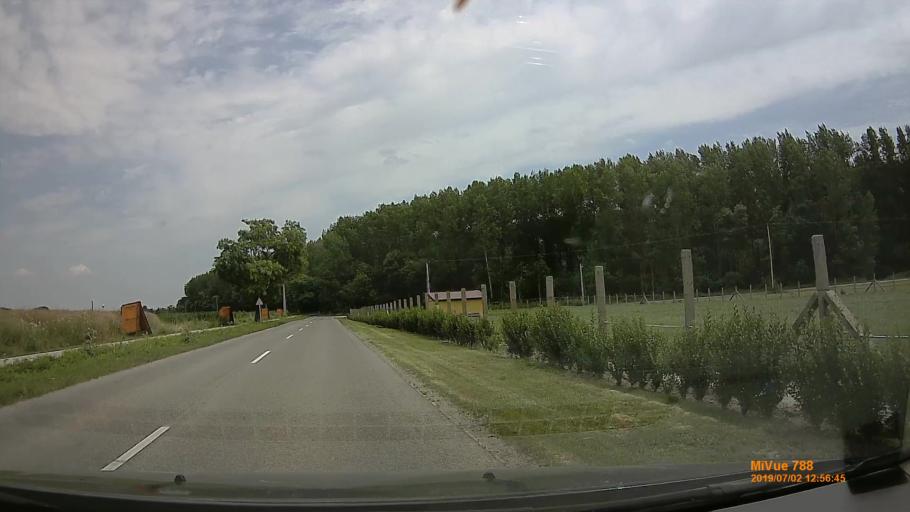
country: HU
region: Gyor-Moson-Sopron
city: Mosonmagyarovar
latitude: 47.8544
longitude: 17.3026
